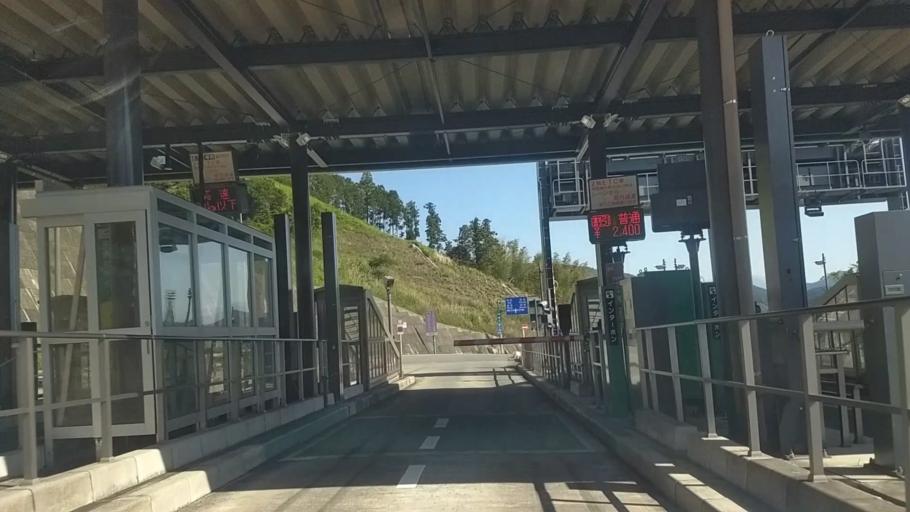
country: JP
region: Shizuoka
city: Fujinomiya
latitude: 35.1495
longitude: 138.5204
